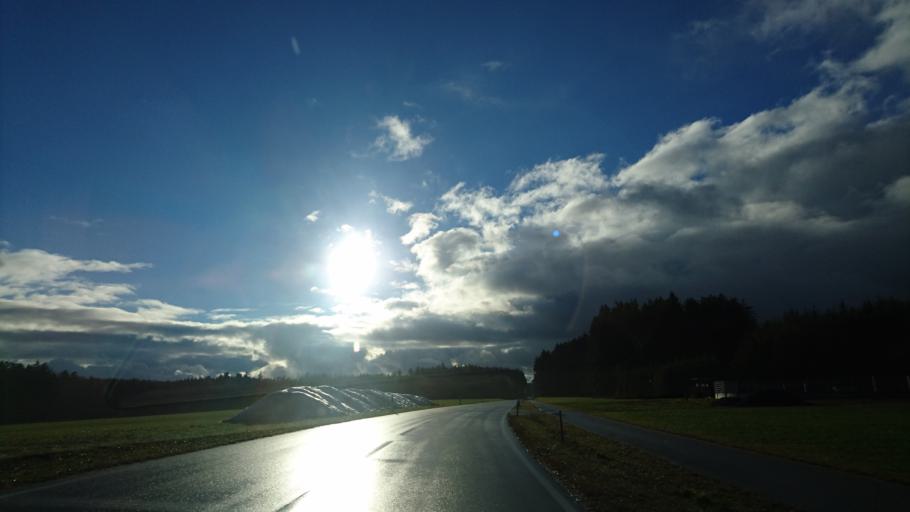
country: DE
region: Bavaria
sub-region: Swabia
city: Heretsried
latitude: 48.4710
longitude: 10.7046
